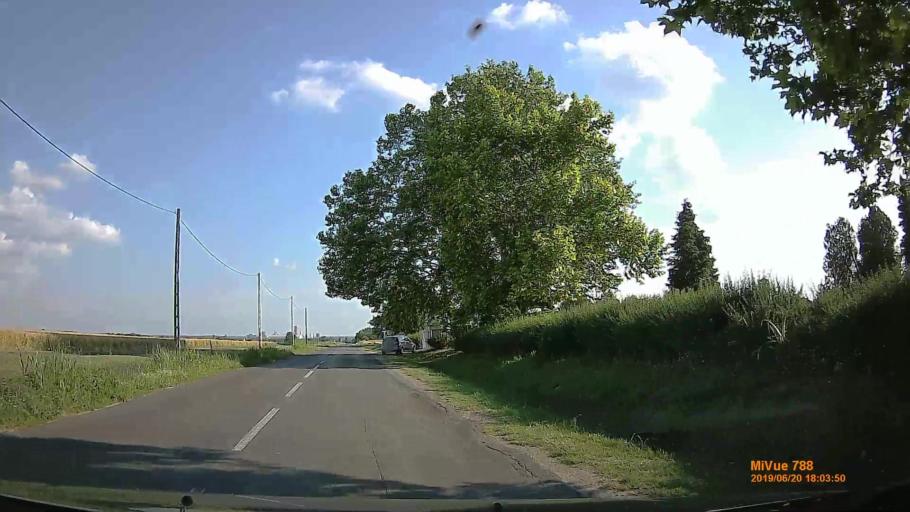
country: HU
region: Baranya
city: Szentlorinc
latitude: 46.0571
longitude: 17.9902
